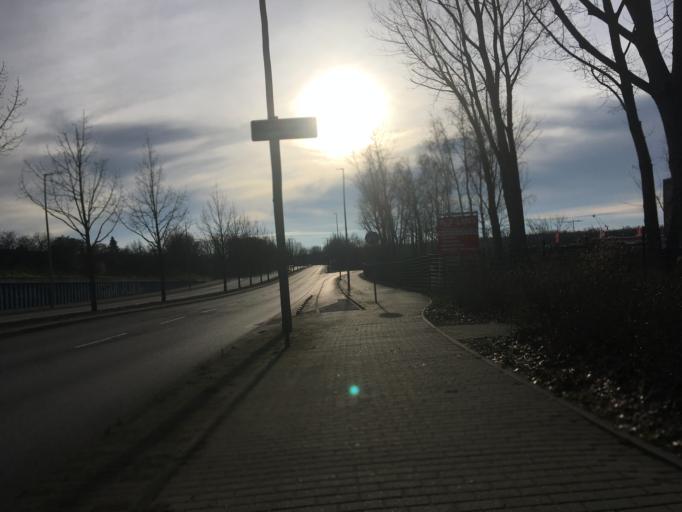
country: DE
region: Berlin
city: Biesdorf
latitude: 52.5123
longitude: 13.5442
